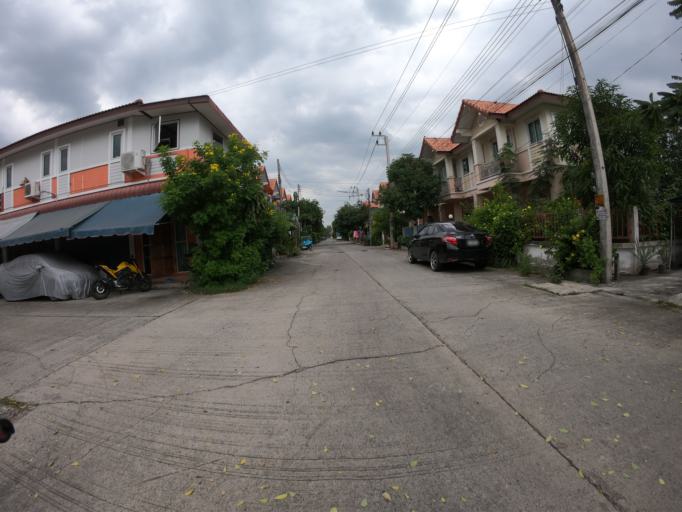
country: TH
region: Pathum Thani
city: Ban Rangsit
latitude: 14.0490
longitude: 100.8347
